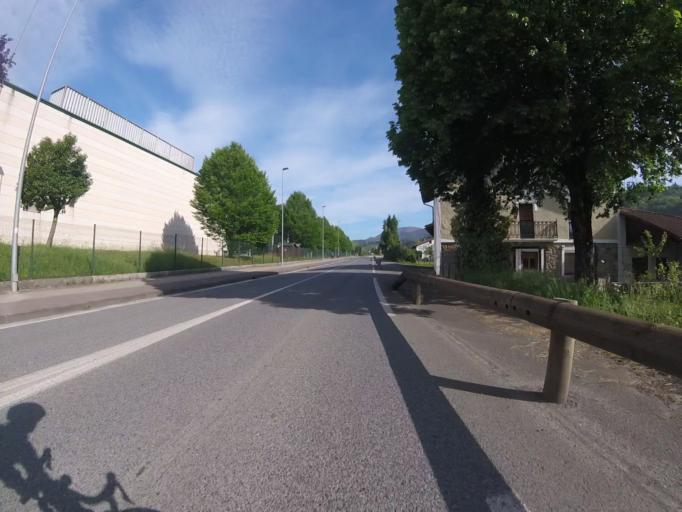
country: ES
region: Basque Country
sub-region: Provincia de Guipuzcoa
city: Ormaiztegui
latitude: 43.0496
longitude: -2.2614
